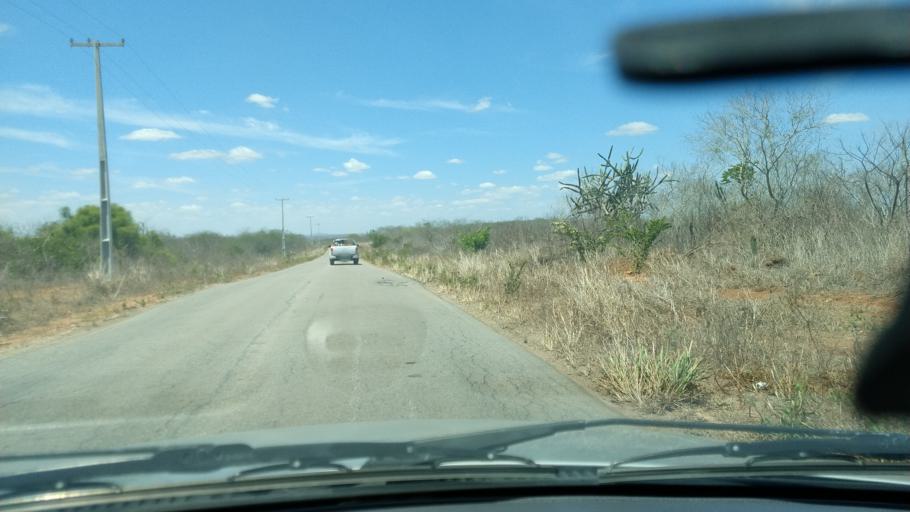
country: BR
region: Rio Grande do Norte
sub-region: Sao Paulo Do Potengi
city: Sao Paulo do Potengi
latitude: -5.9133
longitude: -35.5918
